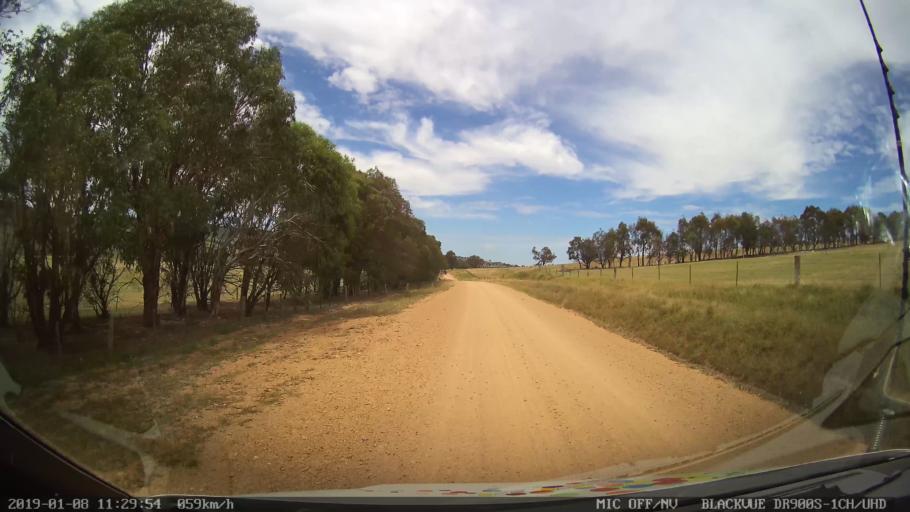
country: AU
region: New South Wales
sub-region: Guyra
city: Guyra
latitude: -30.3037
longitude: 151.5468
